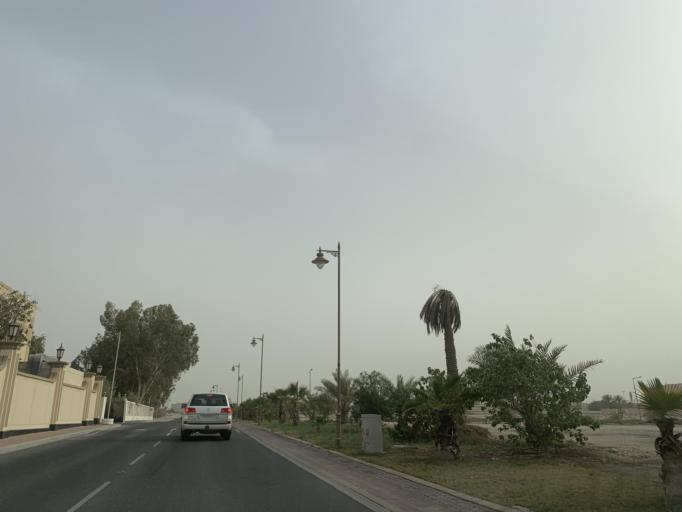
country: BH
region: Northern
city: Ar Rifa'
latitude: 26.1382
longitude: 50.5327
